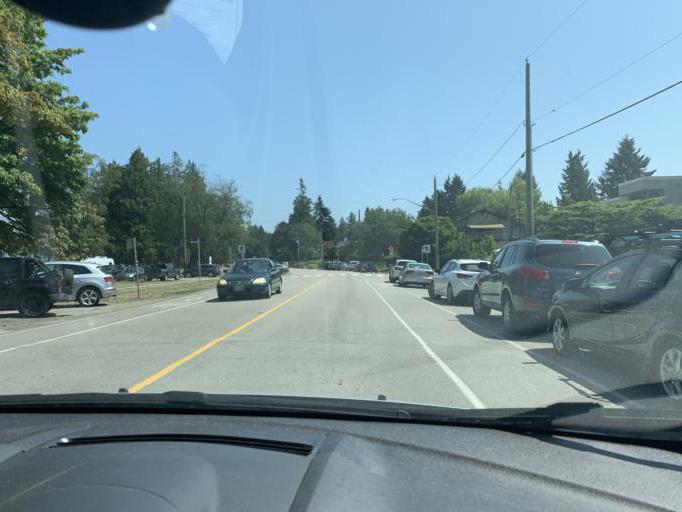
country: CA
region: British Columbia
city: West End
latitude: 49.2744
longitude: -123.2095
